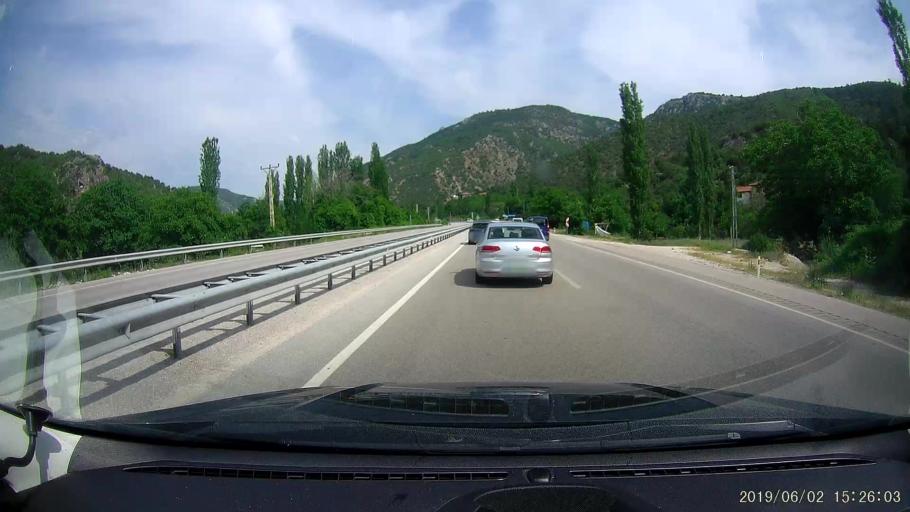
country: TR
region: Amasya
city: Saraycik
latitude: 40.9885
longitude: 35.0301
